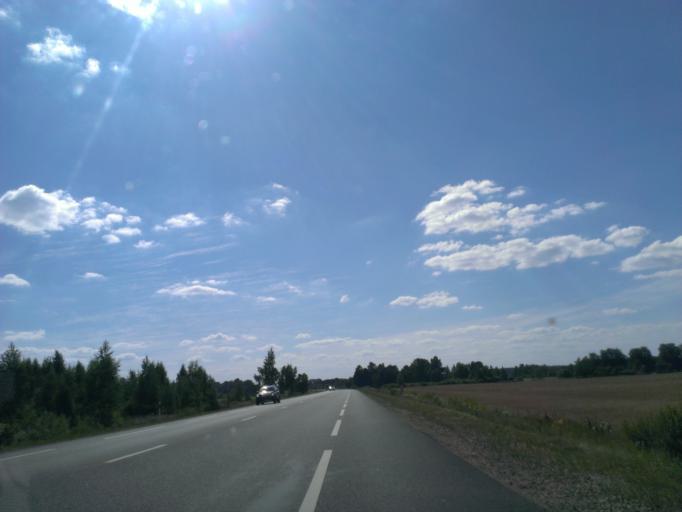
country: LV
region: Adazi
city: Adazi
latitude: 57.1092
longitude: 24.3185
